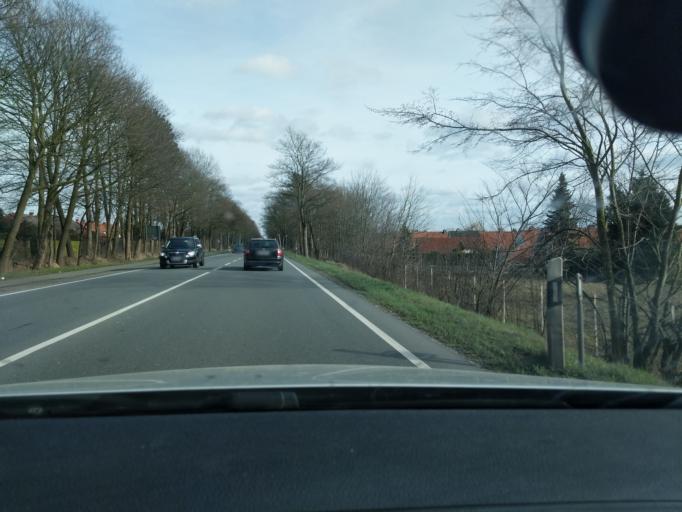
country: DE
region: Lower Saxony
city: Stade
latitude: 53.5832
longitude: 9.4765
